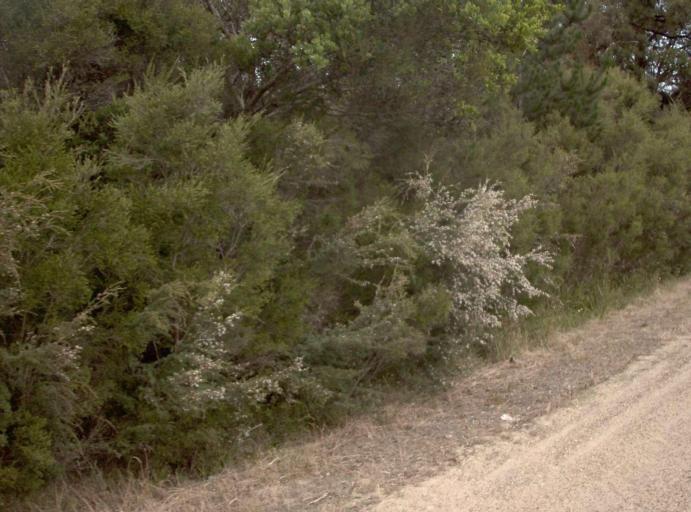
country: AU
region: Victoria
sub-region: Wellington
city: Sale
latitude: -38.1911
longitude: 147.0935
